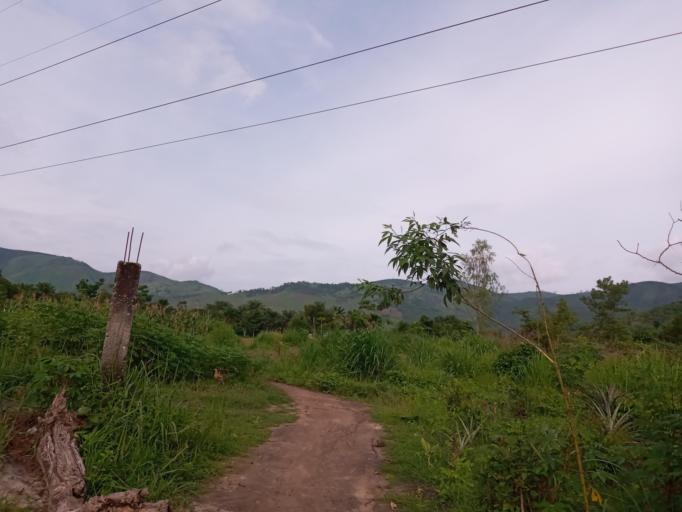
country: SL
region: Northern Province
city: Bumbuna
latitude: 9.0474
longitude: -11.7550
